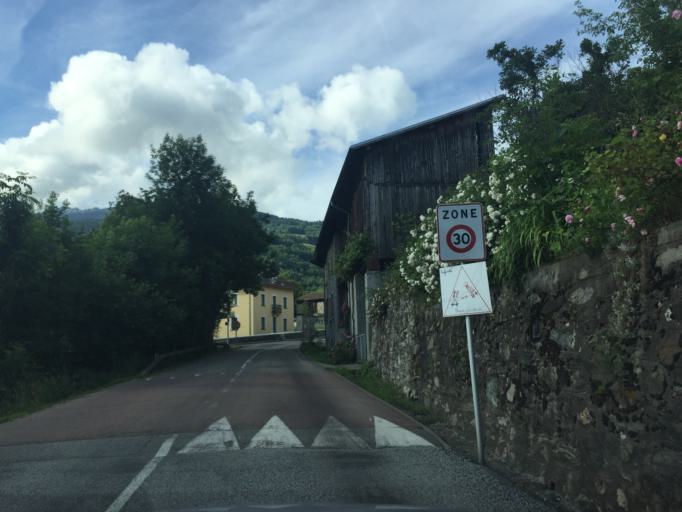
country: FR
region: Rhone-Alpes
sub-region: Departement de la Savoie
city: La Rochette
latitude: 45.4443
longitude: 6.1218
